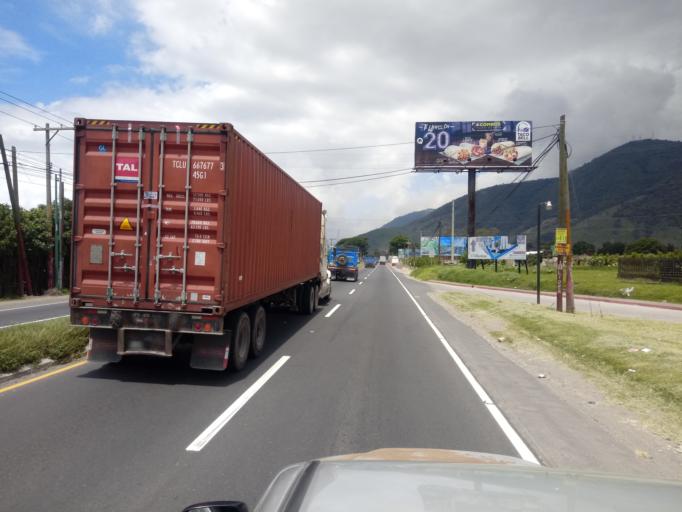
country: GT
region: Guatemala
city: Amatitlan
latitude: 14.4771
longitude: -90.6326
